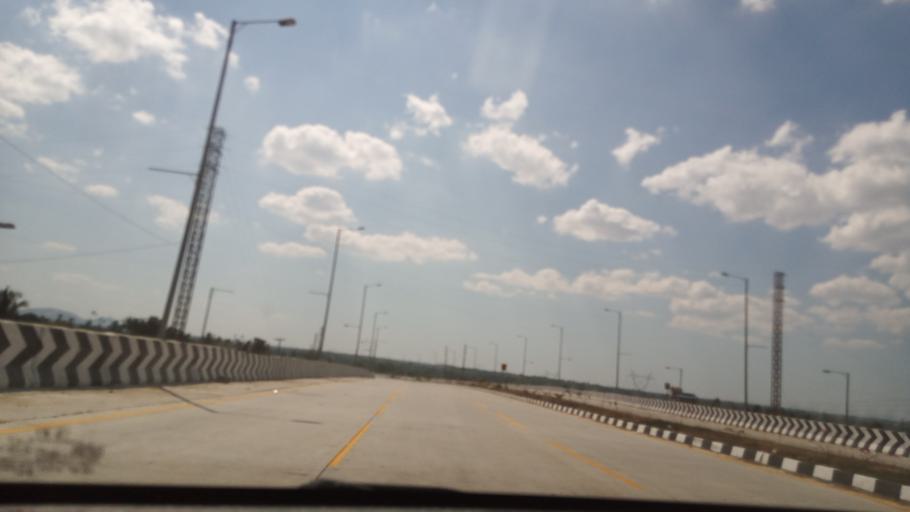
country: IN
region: Andhra Pradesh
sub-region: Chittoor
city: Palmaner
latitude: 13.2213
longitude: 78.7346
